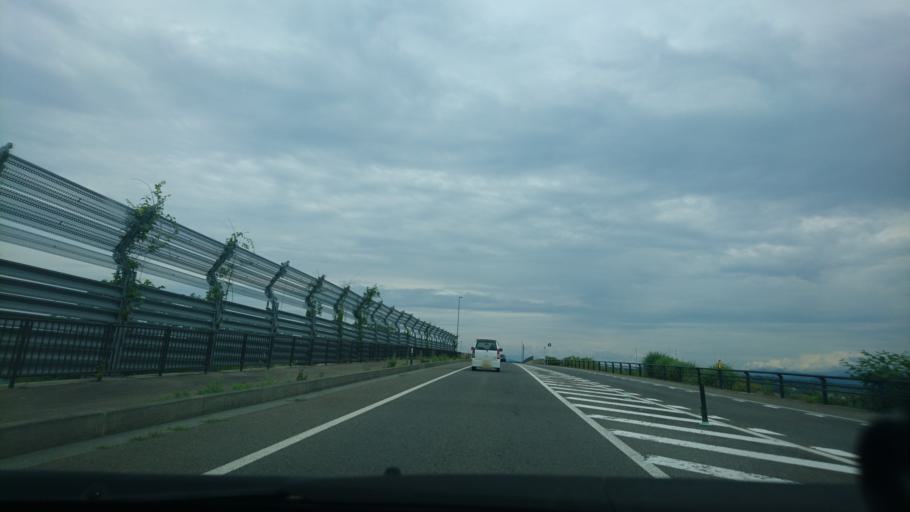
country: JP
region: Akita
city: Omagari
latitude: 39.4901
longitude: 140.4517
